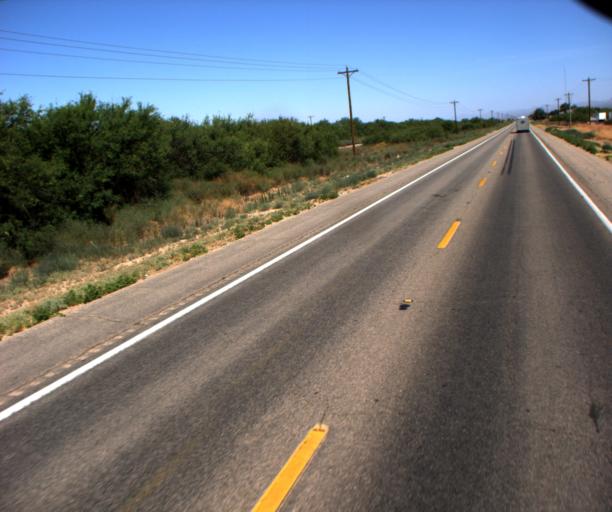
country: US
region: Arizona
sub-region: Graham County
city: Pima
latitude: 32.9551
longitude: -109.9162
